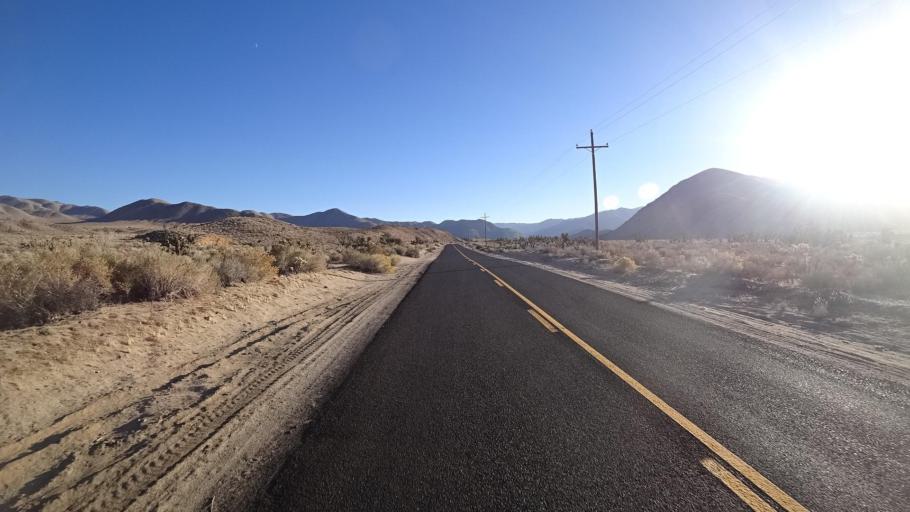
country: US
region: California
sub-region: Kern County
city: Weldon
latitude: 35.6223
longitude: -118.2430
